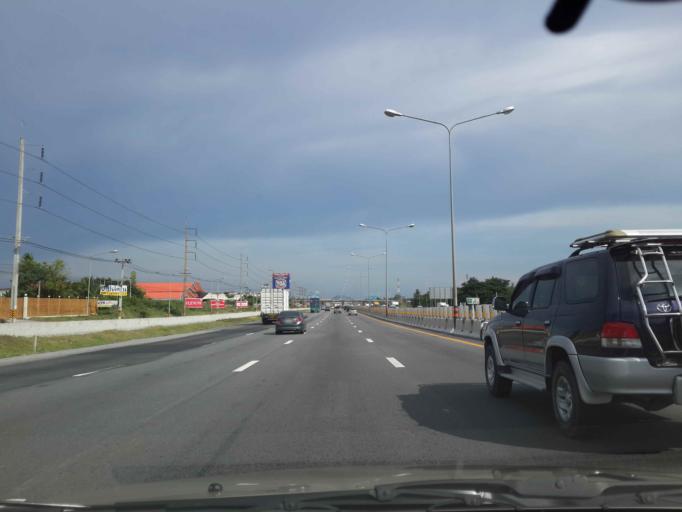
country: TH
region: Chon Buri
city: Si Racha
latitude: 13.2426
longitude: 100.9962
